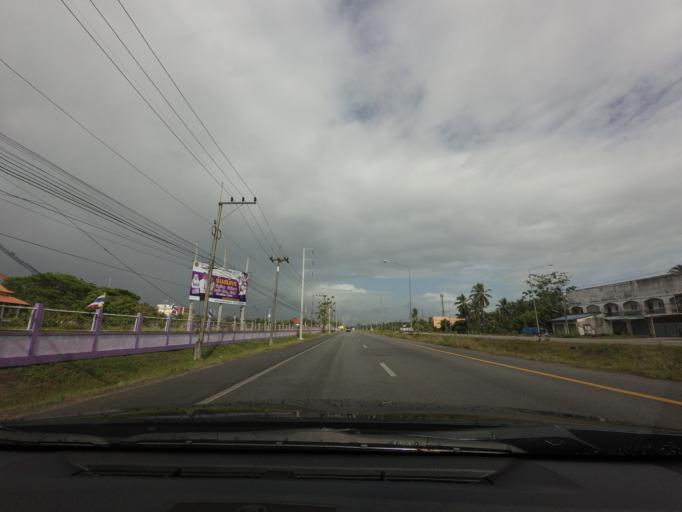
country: TH
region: Pattani
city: Nong Chik
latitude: 6.8076
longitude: 101.1195
